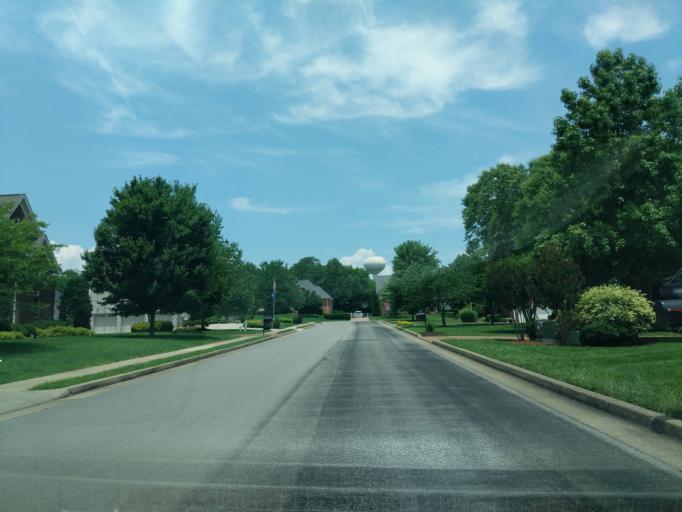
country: US
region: Tennessee
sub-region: Davidson County
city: Lakewood
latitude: 36.2324
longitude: -86.6293
